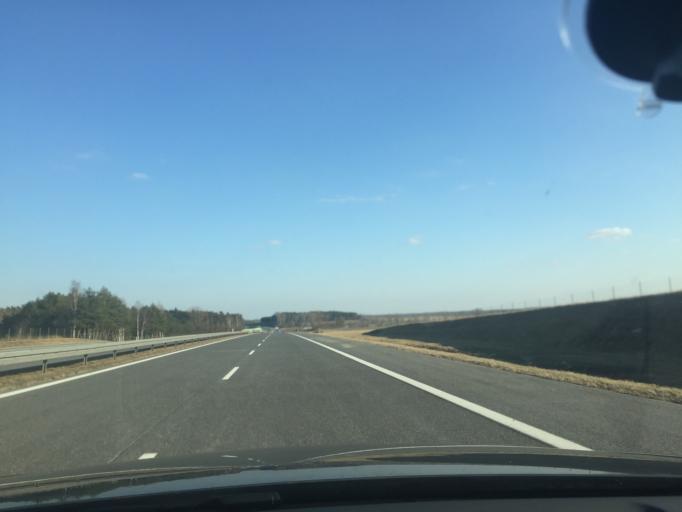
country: PL
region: Lubusz
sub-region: Powiat miedzyrzecki
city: Brojce
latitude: 52.3039
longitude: 15.6383
